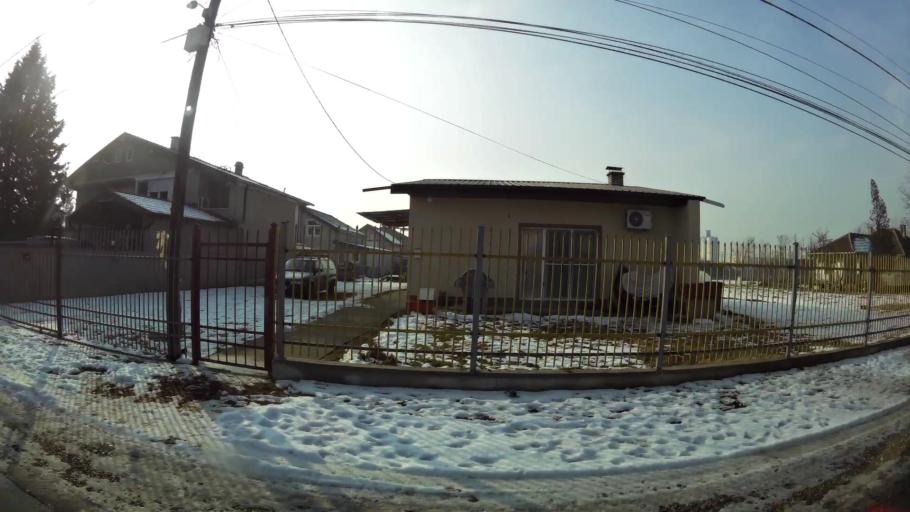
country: MK
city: Kadino
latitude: 41.9734
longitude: 21.5979
